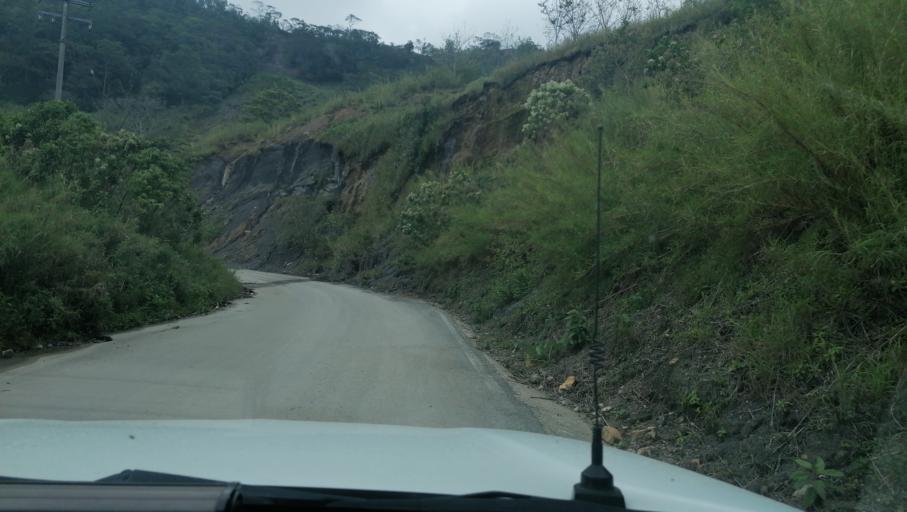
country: MX
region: Chiapas
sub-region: Ocotepec
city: San Pablo Huacano
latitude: 17.2637
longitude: -93.2655
